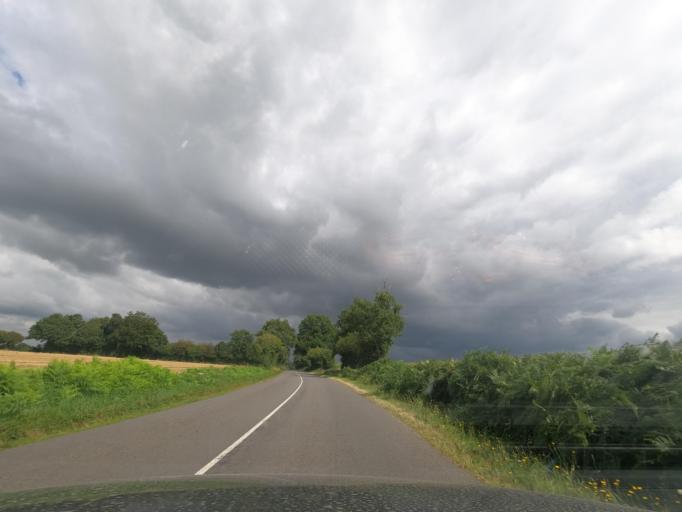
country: FR
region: Lower Normandy
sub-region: Departement de l'Orne
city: Briouze
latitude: 48.6921
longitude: -0.4220
